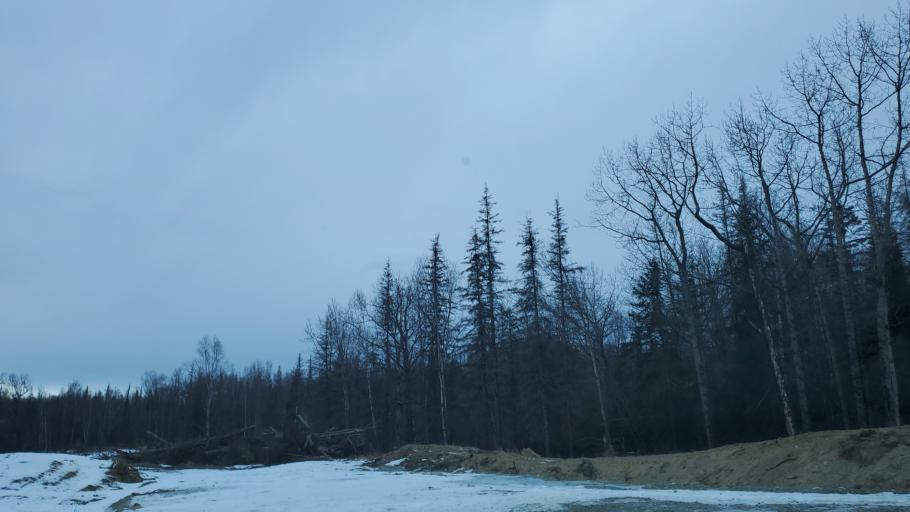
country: US
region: Alaska
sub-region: Matanuska-Susitna Borough
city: Gateway
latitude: 61.6535
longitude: -149.2332
